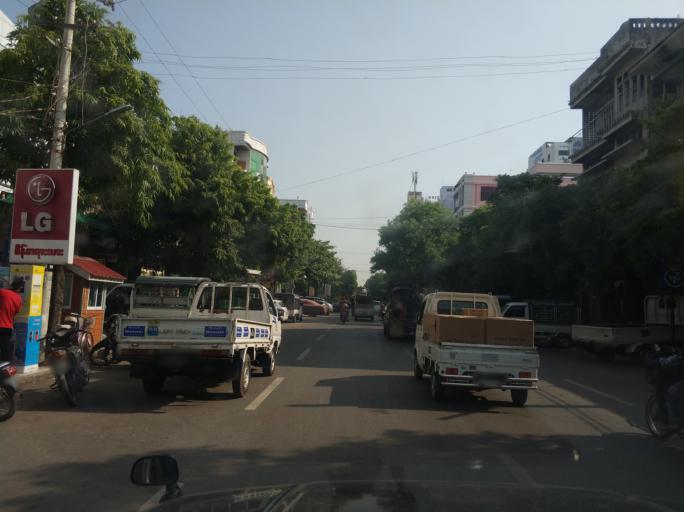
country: MM
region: Mandalay
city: Mandalay
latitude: 21.9794
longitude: 96.0793
